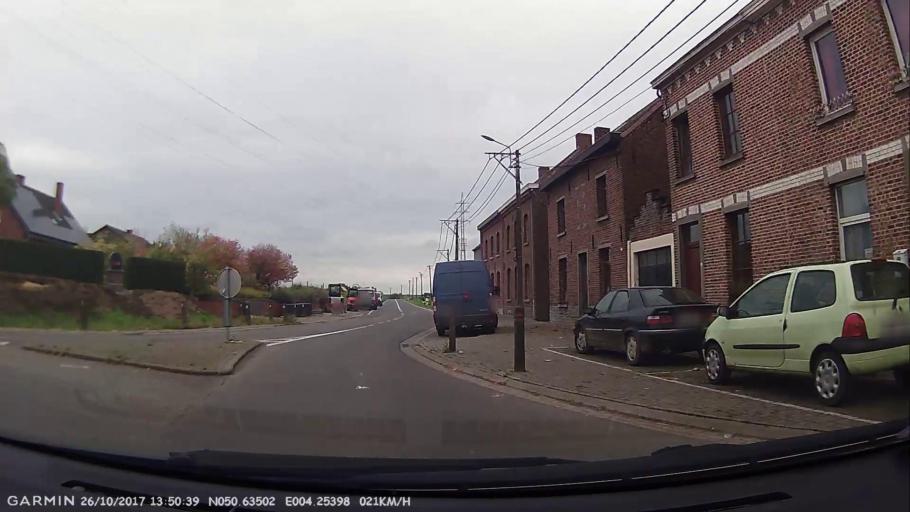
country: BE
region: Wallonia
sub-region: Province du Brabant Wallon
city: Ittre
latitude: 50.6350
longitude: 4.2541
